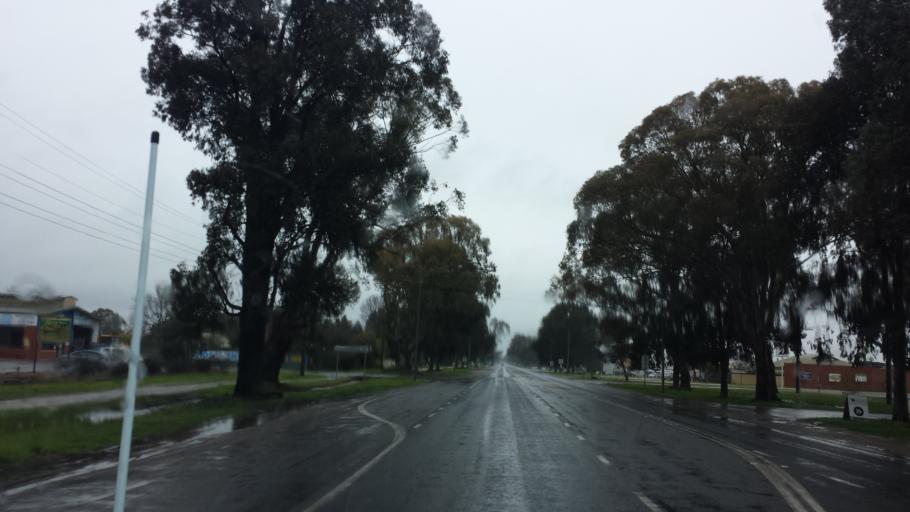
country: AU
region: Victoria
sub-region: Benalla
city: Benalla
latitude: -36.5466
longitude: 146.0018
